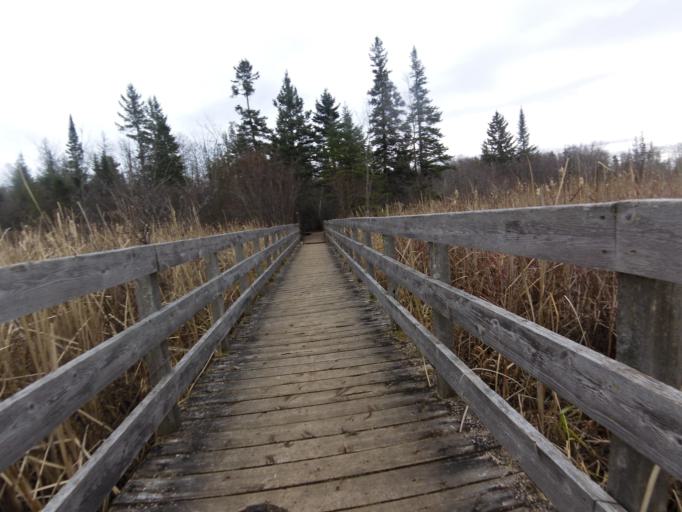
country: CA
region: Ontario
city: Bells Corners
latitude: 45.2917
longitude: -75.8133
